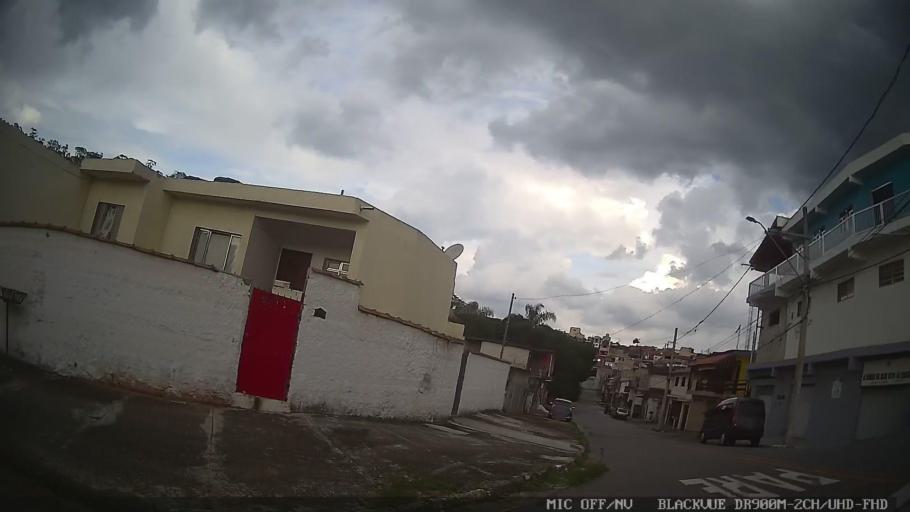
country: BR
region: Sao Paulo
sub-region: Ribeirao Pires
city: Ribeirao Pires
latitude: -23.6794
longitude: -46.4142
